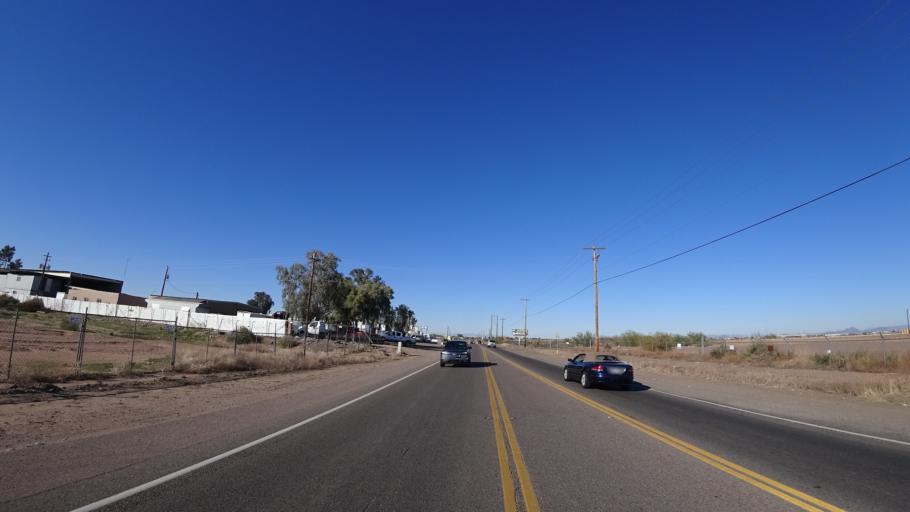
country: US
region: Arizona
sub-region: Maricopa County
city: Laveen
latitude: 33.3929
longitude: -112.2031
